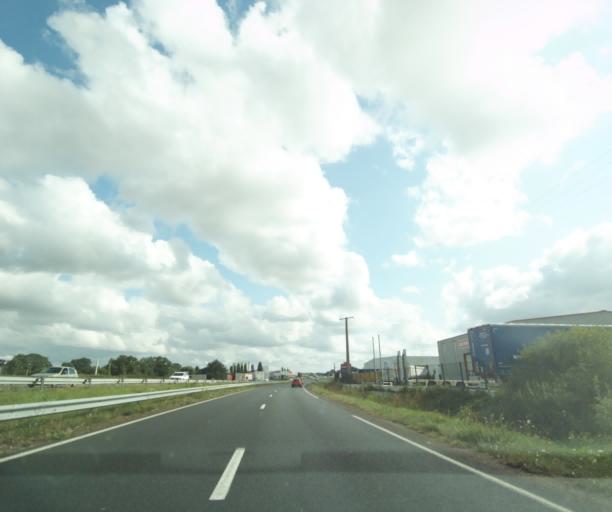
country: FR
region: Pays de la Loire
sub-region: Departement de la Vendee
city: Mouilleron-le-Captif
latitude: 46.7388
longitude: -1.4305
